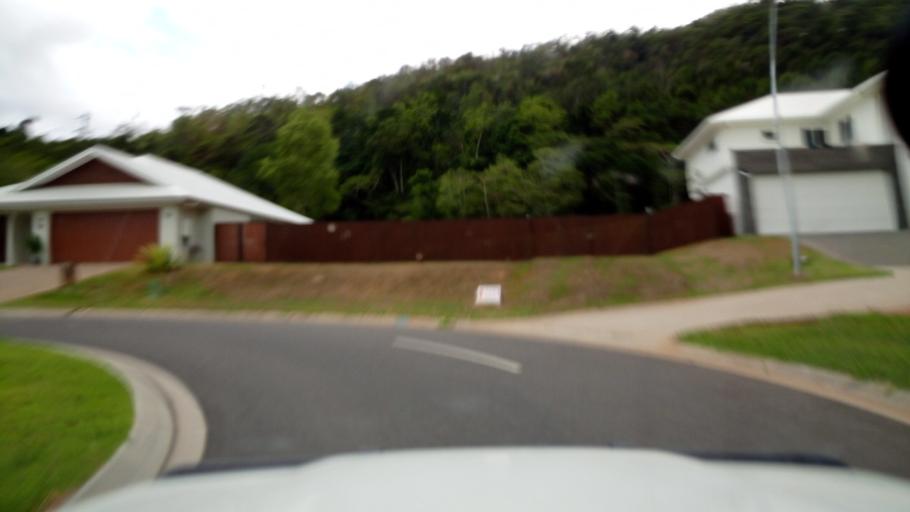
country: AU
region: Queensland
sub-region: Cairns
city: Redlynch
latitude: -16.8449
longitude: 145.6882
